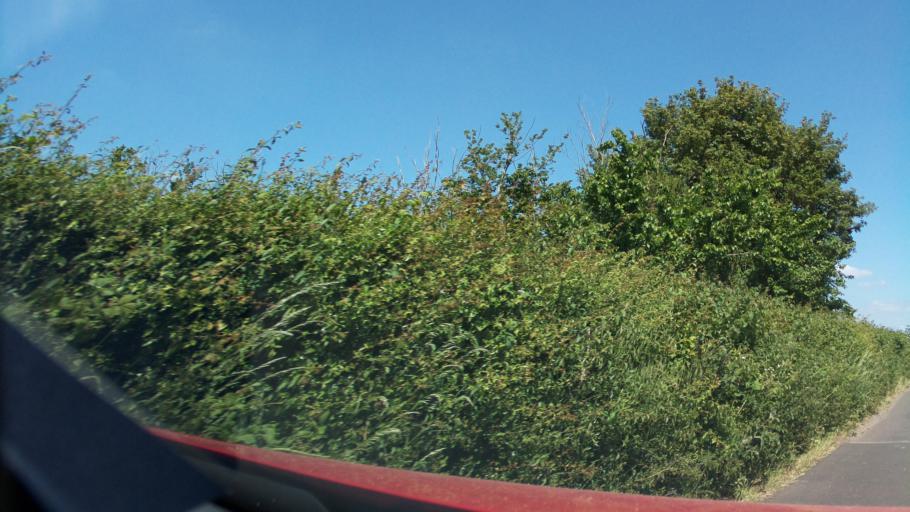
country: GB
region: England
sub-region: Wiltshire
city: Lyneham
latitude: 51.4923
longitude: -1.9283
